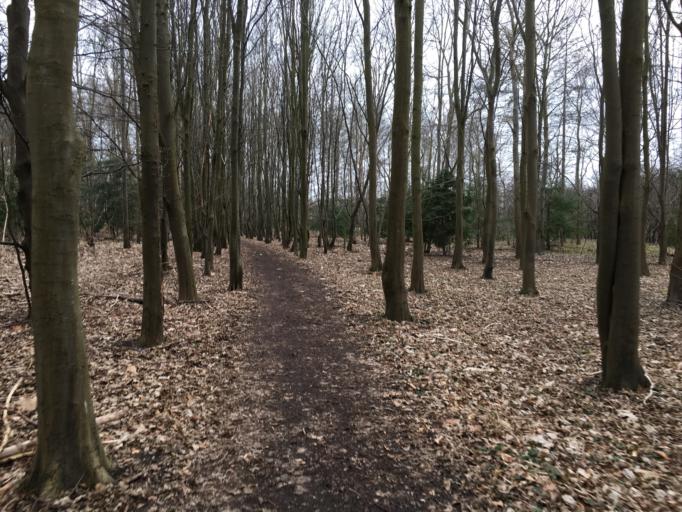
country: SE
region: Skane
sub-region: Lomma Kommun
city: Lomma
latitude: 55.6533
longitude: 13.0749
